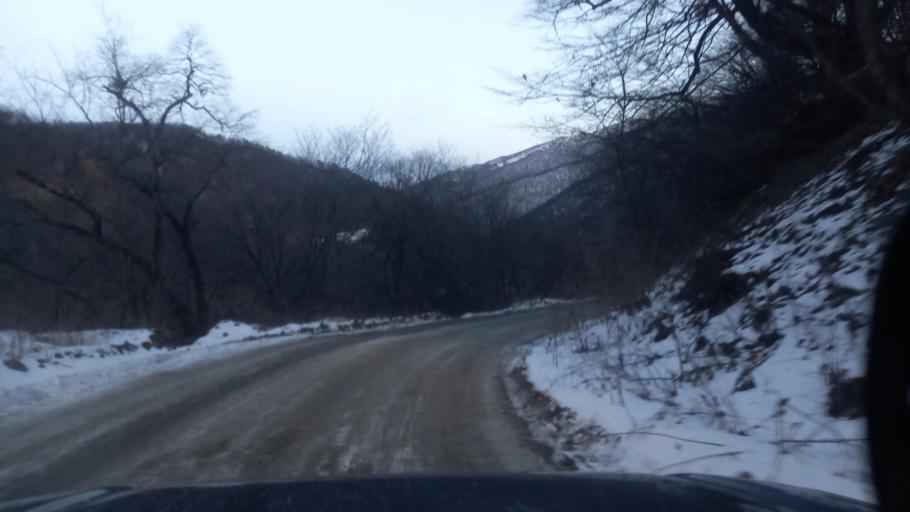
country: RU
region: Ingushetiya
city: Dzhayrakh
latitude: 42.8308
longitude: 44.5853
